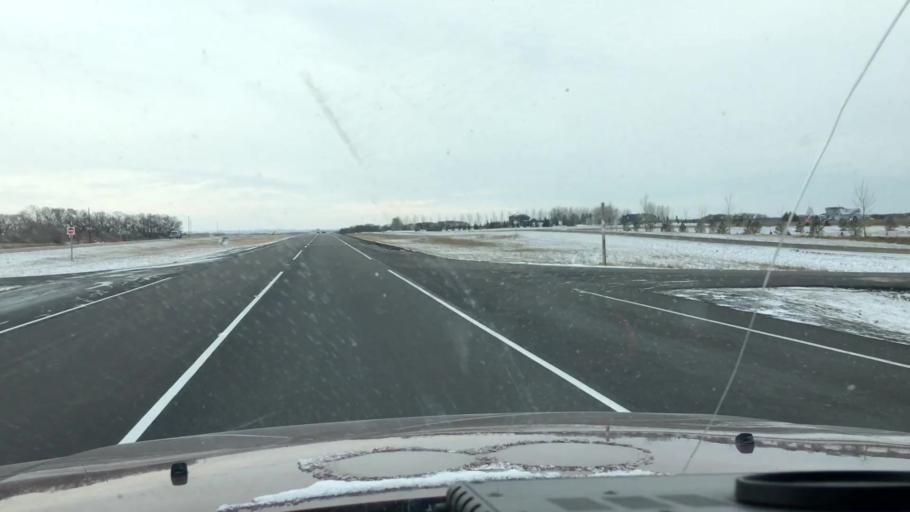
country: CA
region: Saskatchewan
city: Saskatoon
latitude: 51.9109
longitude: -106.5265
